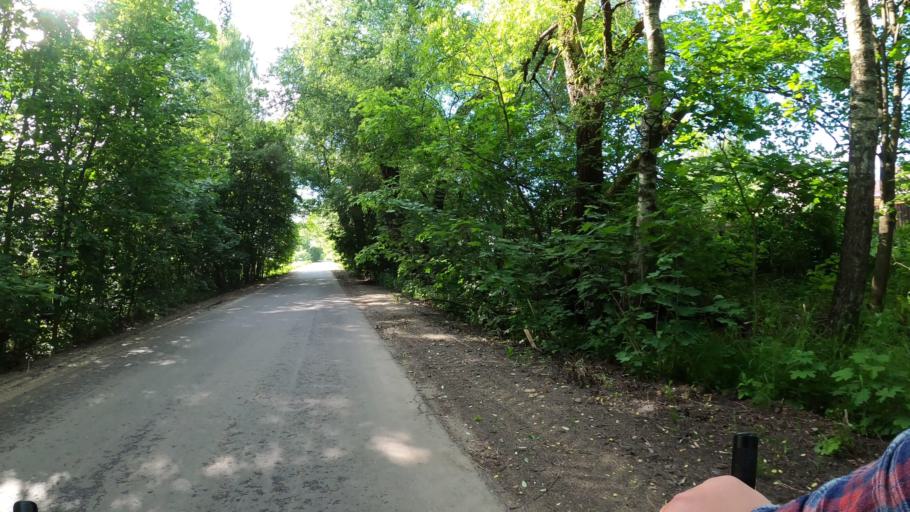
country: RU
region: Moskovskaya
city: Ashitkovo
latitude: 55.4390
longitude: 38.6319
